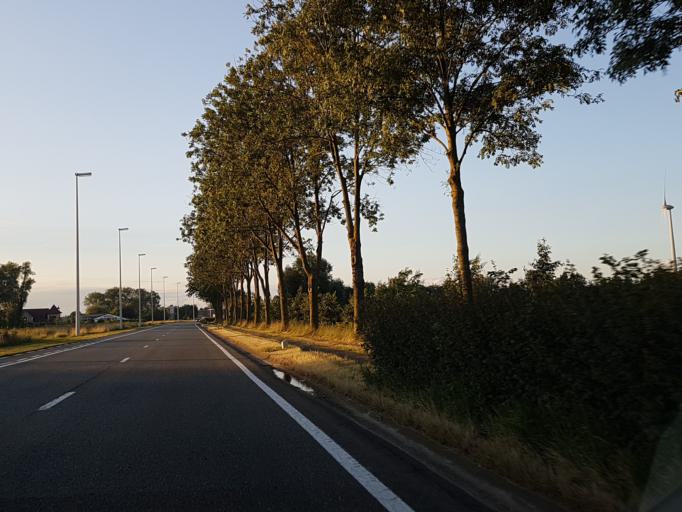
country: BE
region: Flanders
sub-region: Provincie Oost-Vlaanderen
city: Hamme
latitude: 51.0673
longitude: 4.1240
